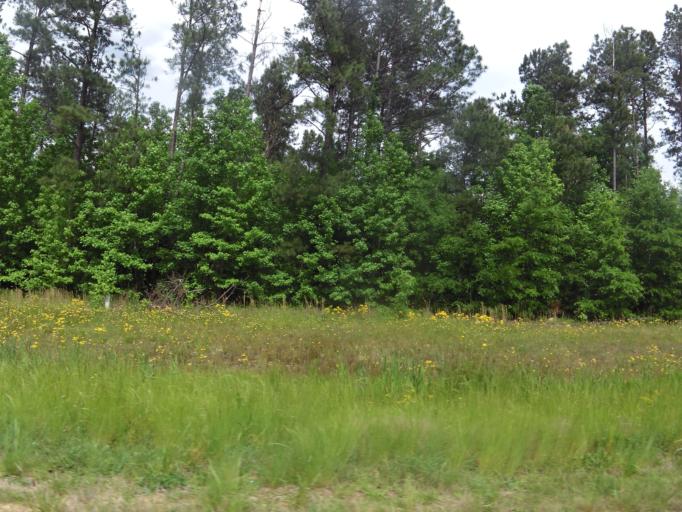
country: US
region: Georgia
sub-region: McDuffie County
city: Thomson
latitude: 33.4361
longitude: -82.4898
